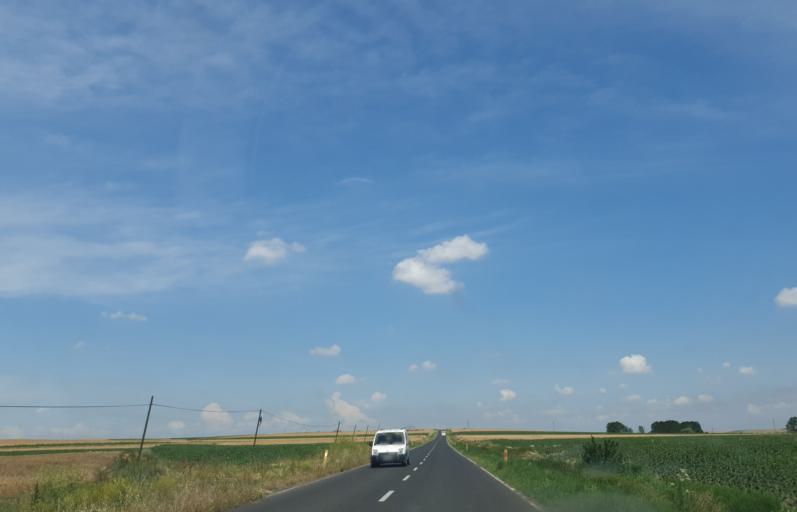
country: TR
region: Kirklareli
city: Buyukkaristiran
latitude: 41.2266
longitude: 27.5625
